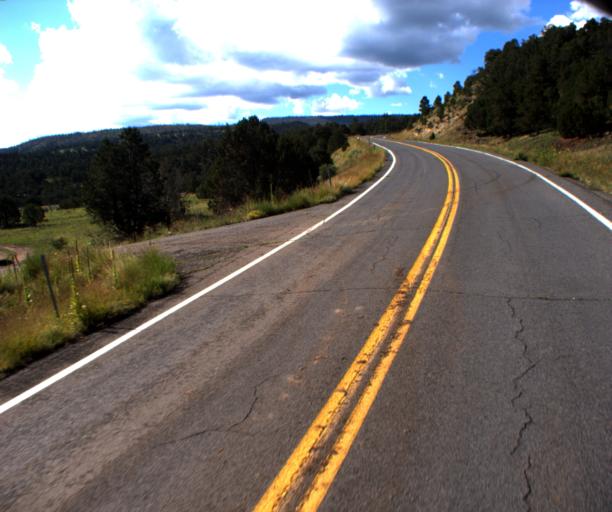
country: US
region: Arizona
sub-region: Apache County
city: Eagar
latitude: 34.0874
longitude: -109.3437
